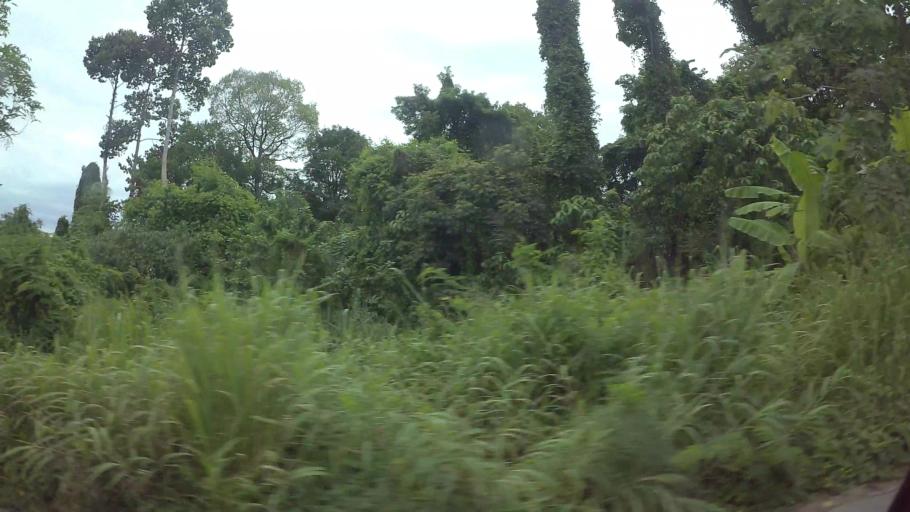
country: TH
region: Chon Buri
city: Si Racha
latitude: 13.1859
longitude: 100.9842
